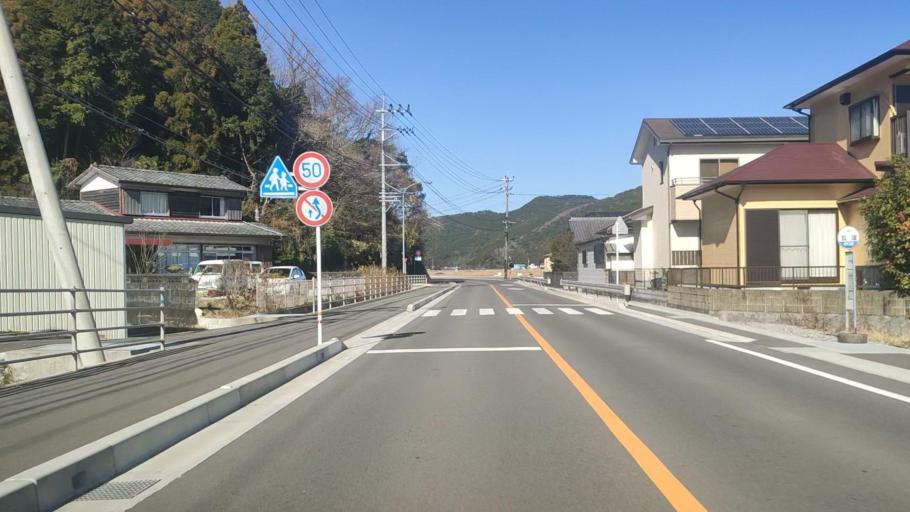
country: JP
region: Oita
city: Saiki
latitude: 32.9234
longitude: 131.9264
